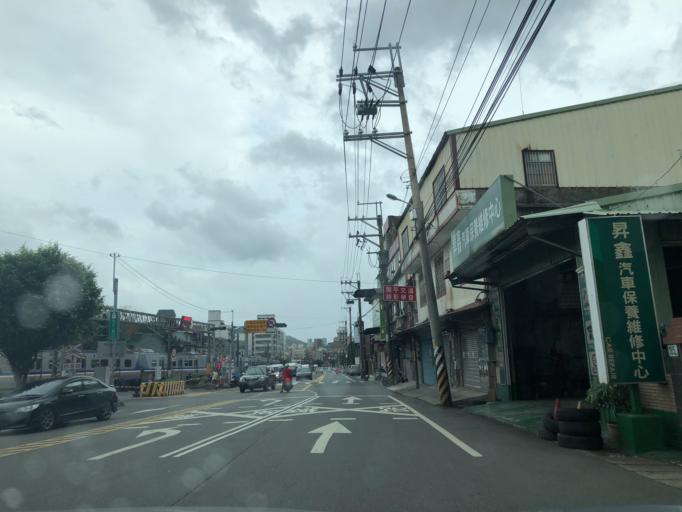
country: TW
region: Taiwan
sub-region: Taoyuan
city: Taoyuan
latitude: 24.9479
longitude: 121.3413
